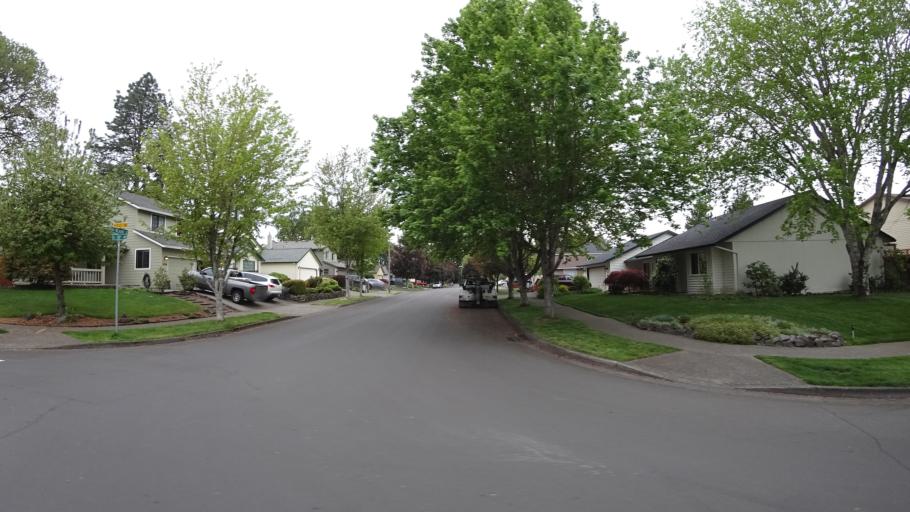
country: US
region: Oregon
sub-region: Washington County
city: Aloha
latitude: 45.5057
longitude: -122.9093
